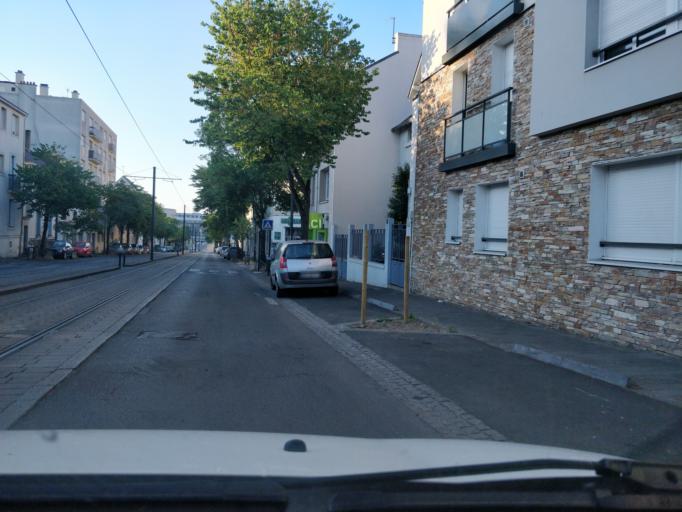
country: FR
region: Pays de la Loire
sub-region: Departement de la Loire-Atlantique
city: Nantes
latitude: 47.2302
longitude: -1.5558
